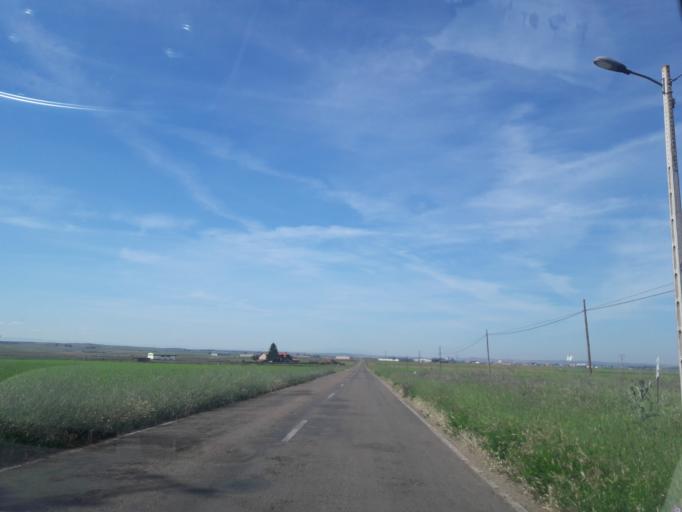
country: ES
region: Castille and Leon
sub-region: Provincia de Salamanca
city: Villoruela
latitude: 41.0041
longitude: -5.3979
